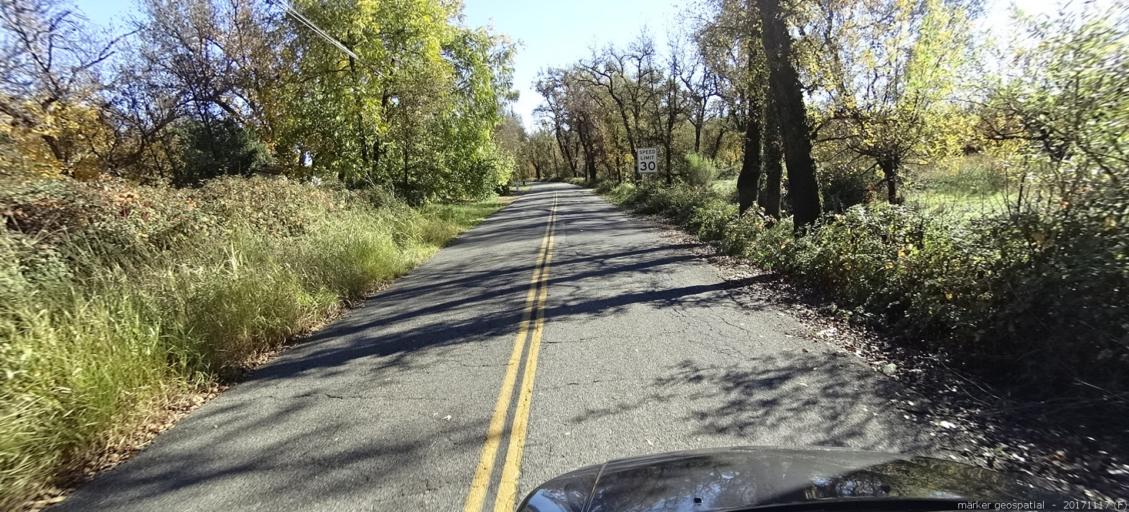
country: US
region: California
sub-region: Shasta County
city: Anderson
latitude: 40.4462
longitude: -122.2480
